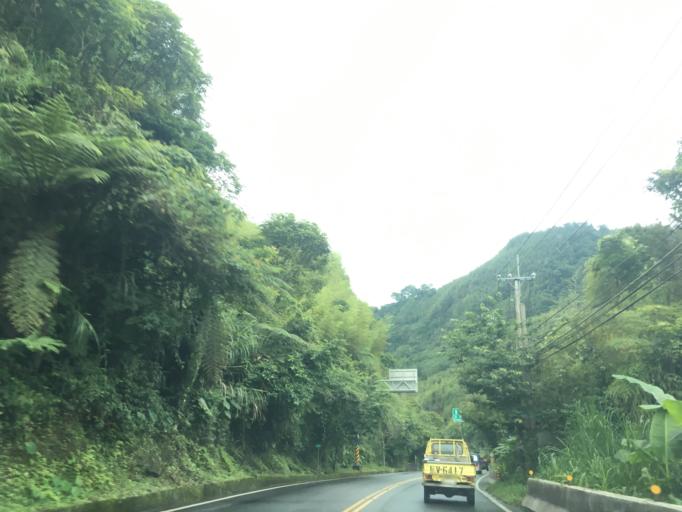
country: TW
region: Taiwan
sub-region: Chiayi
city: Jiayi Shi
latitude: 23.4399
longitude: 120.6686
